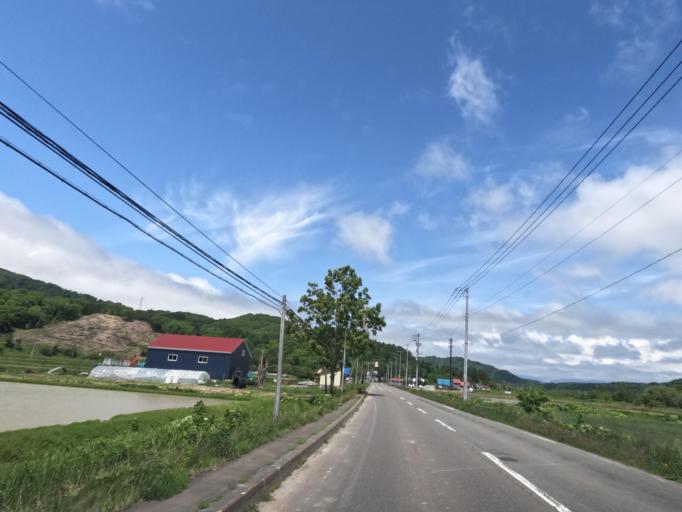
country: JP
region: Hokkaido
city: Tobetsu
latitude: 43.2928
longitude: 141.5400
